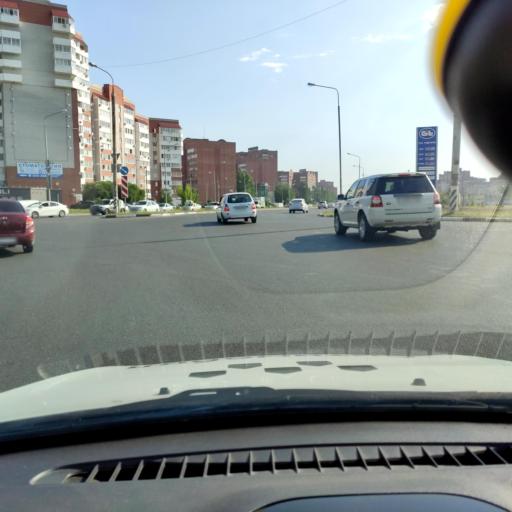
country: RU
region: Samara
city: Tol'yatti
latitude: 53.5313
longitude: 49.3459
